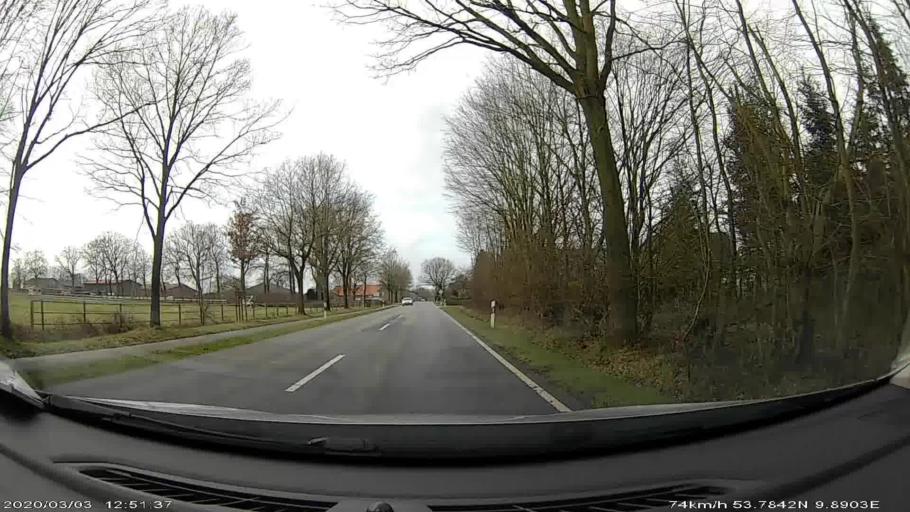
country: DE
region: Schleswig-Holstein
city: Bilsen
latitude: 53.7844
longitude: 9.8875
